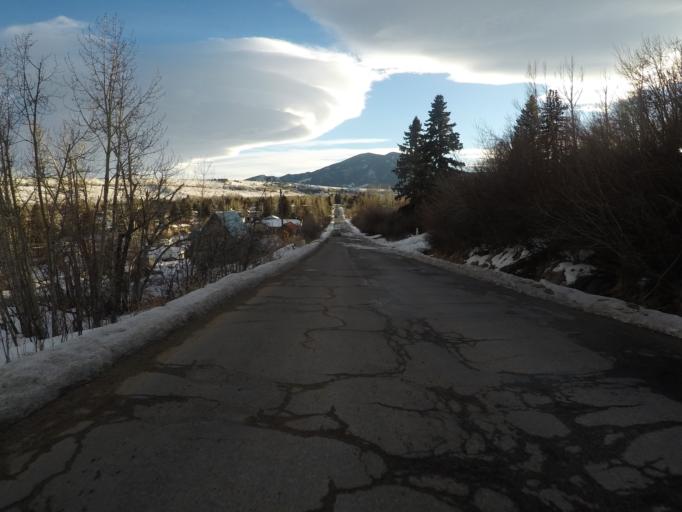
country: US
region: Montana
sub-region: Carbon County
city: Red Lodge
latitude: 45.1812
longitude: -109.2548
